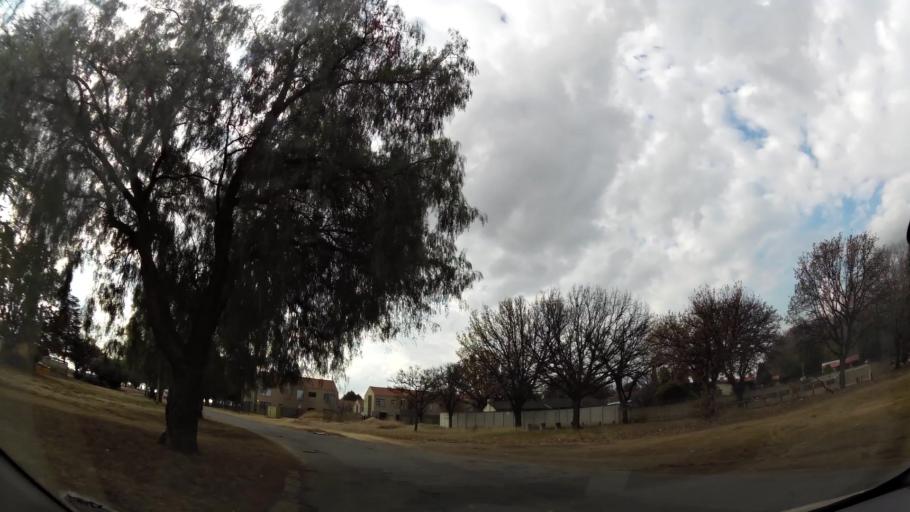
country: ZA
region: Orange Free State
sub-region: Fezile Dabi District Municipality
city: Sasolburg
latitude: -26.7983
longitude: 27.8090
